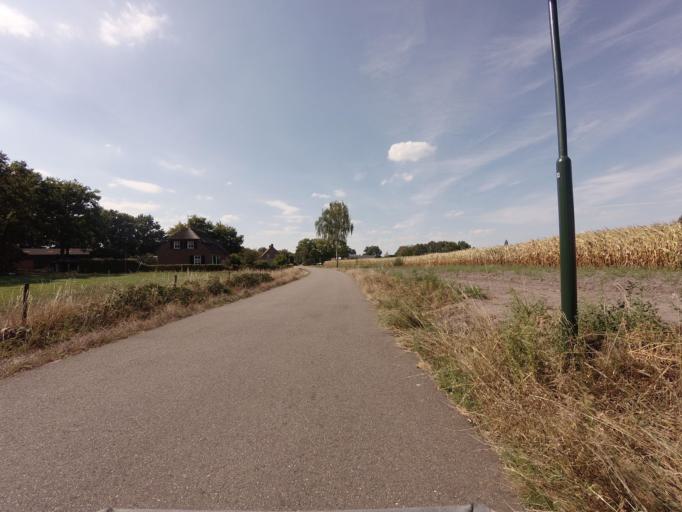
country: NL
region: North Brabant
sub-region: Gemeente Cranendonck
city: Cranendonck
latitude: 51.3000
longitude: 5.5666
